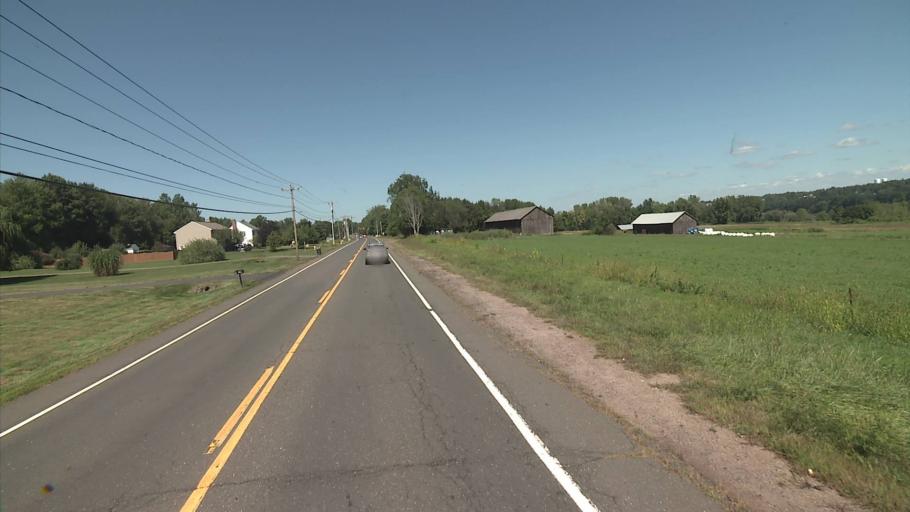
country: US
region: Connecticut
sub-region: Hartford County
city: Enfield
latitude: 41.9793
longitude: -72.6136
